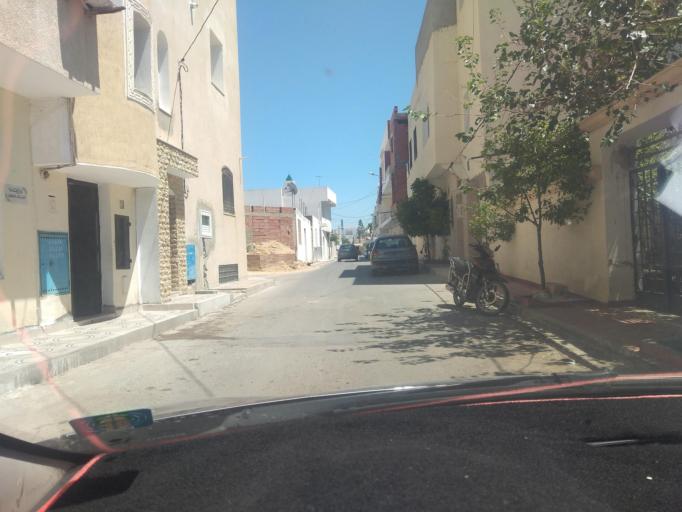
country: TN
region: Susah
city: Hammam Sousse
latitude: 35.8515
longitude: 10.5909
